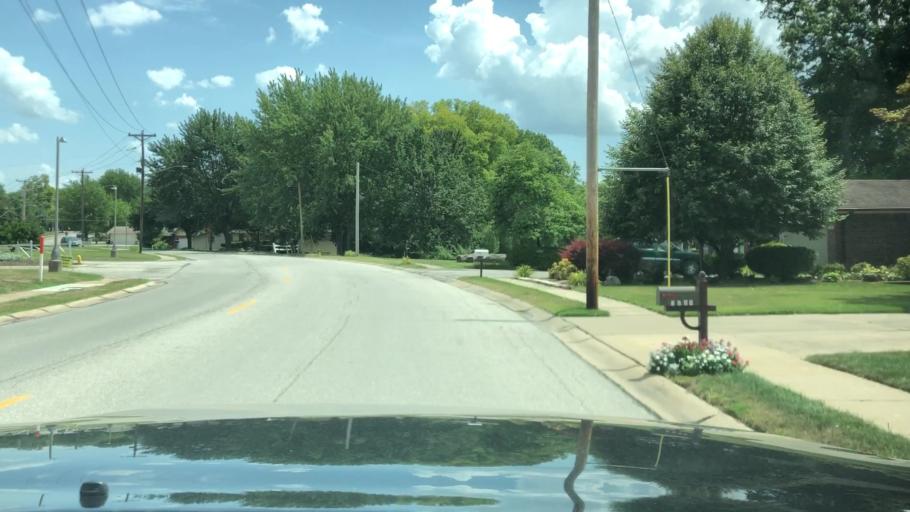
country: US
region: Missouri
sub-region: Saint Charles County
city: Saint Charles
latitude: 38.7947
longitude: -90.5234
